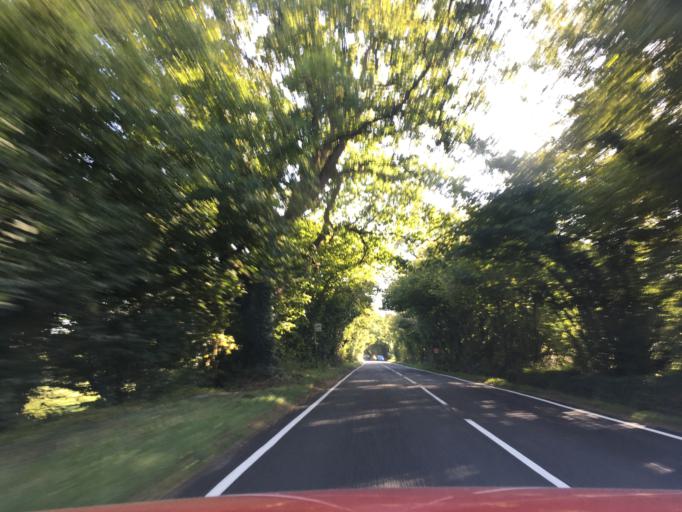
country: GB
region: England
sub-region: Hampshire
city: Four Marks
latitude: 51.0267
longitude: -1.0766
